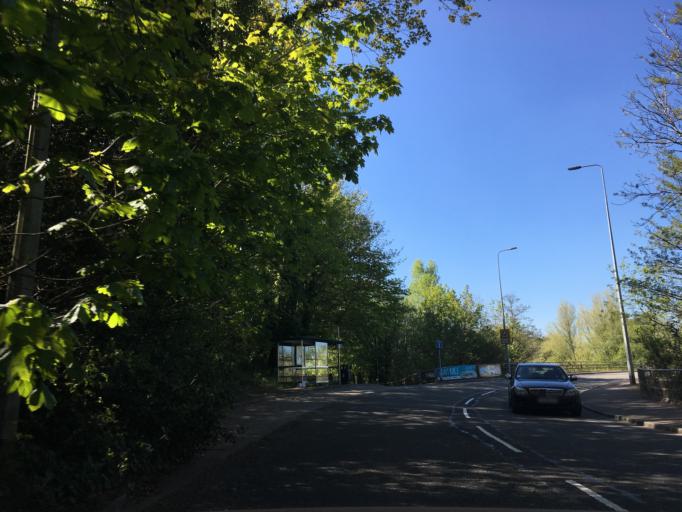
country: GB
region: Wales
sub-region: Cardiff
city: Radyr
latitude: 51.4994
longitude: -3.2272
